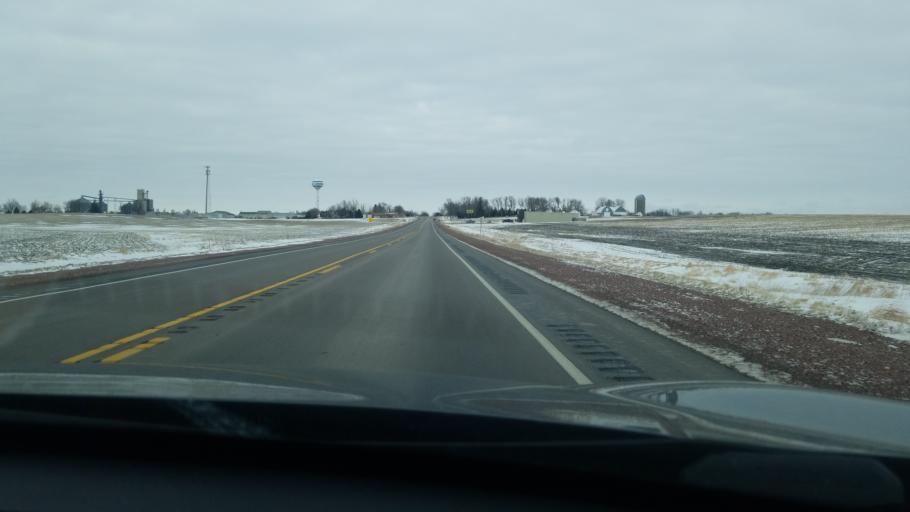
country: US
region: South Dakota
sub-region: Minnehaha County
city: Brandon
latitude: 43.4410
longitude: -96.4293
